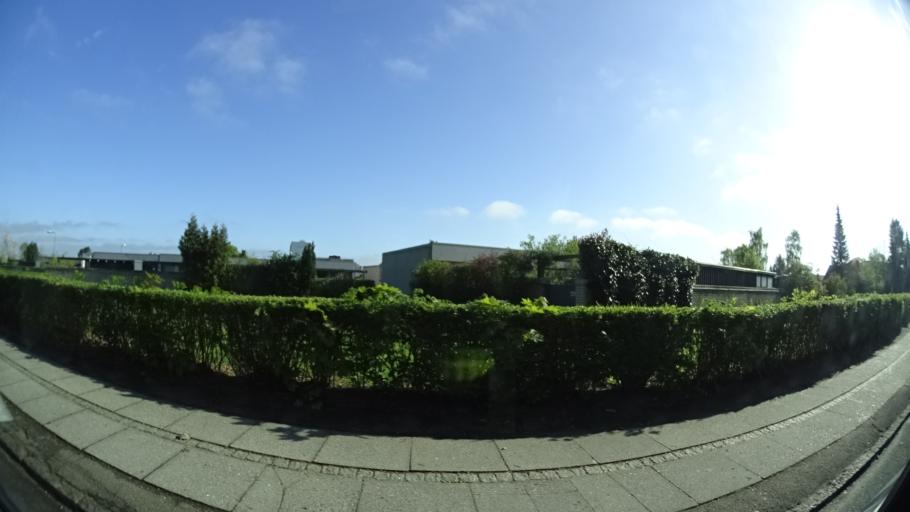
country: DK
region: Central Jutland
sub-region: Arhus Kommune
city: Stavtrup
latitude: 56.1200
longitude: 10.1387
